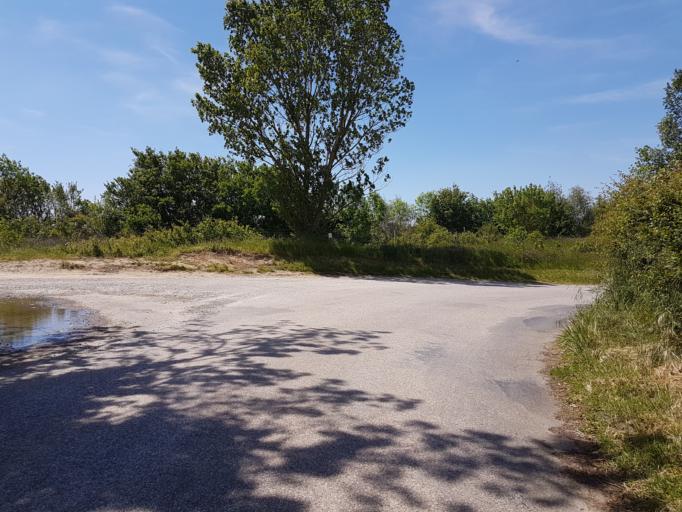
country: FR
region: Rhone-Alpes
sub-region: Departement du Rhone
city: Jons
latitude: 45.7866
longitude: 5.0813
